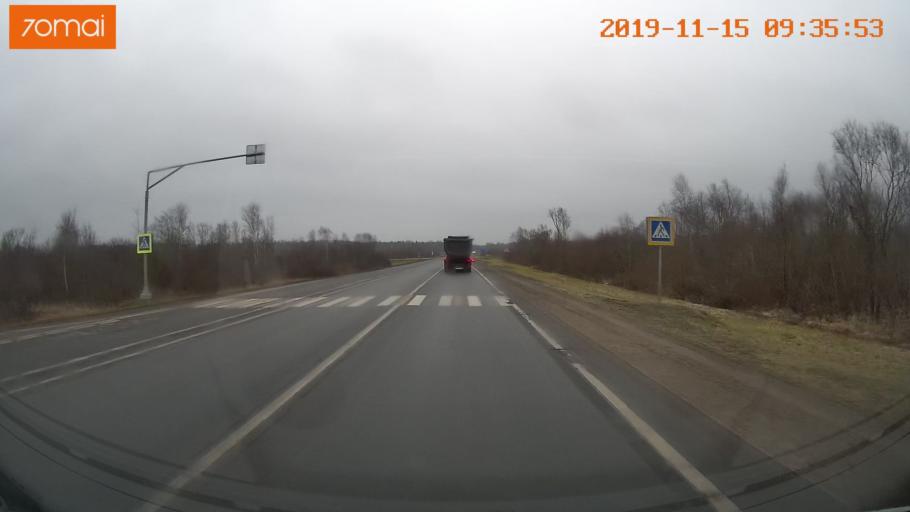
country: RU
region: Vologda
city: Sheksna
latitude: 59.2519
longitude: 38.4079
